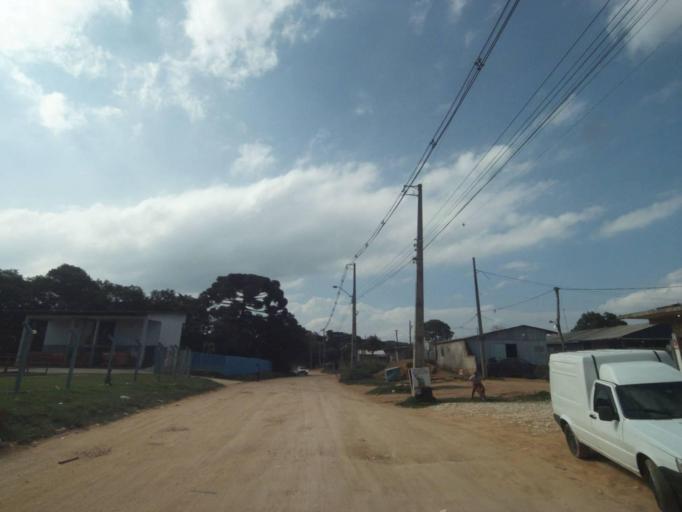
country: BR
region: Parana
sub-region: Araucaria
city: Araucaria
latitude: -25.5120
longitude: -49.3522
